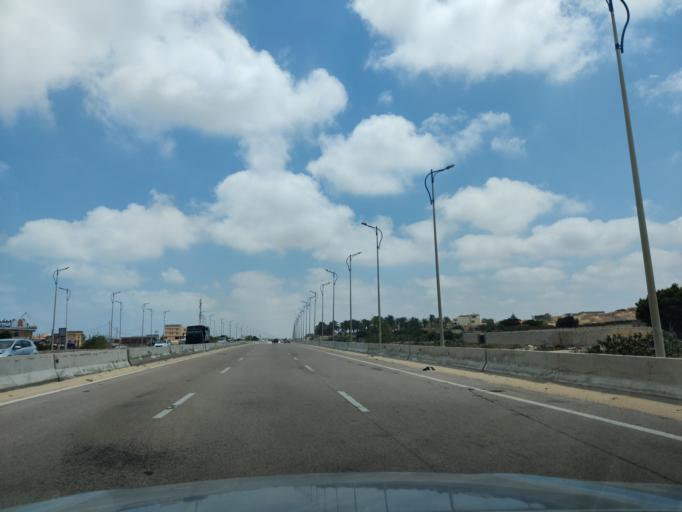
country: EG
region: Alexandria
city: Alexandria
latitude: 30.9791
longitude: 29.5759
